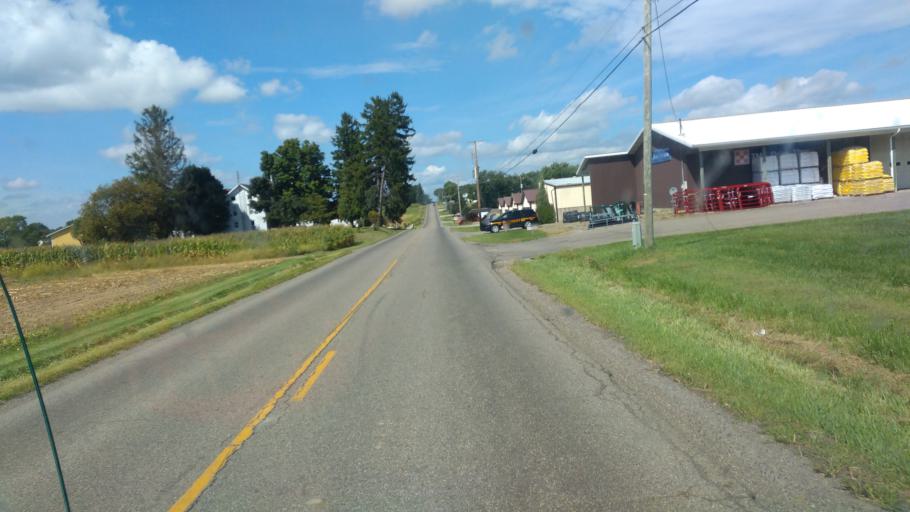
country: US
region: Ohio
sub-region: Holmes County
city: Millersburg
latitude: 40.5674
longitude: -81.8207
